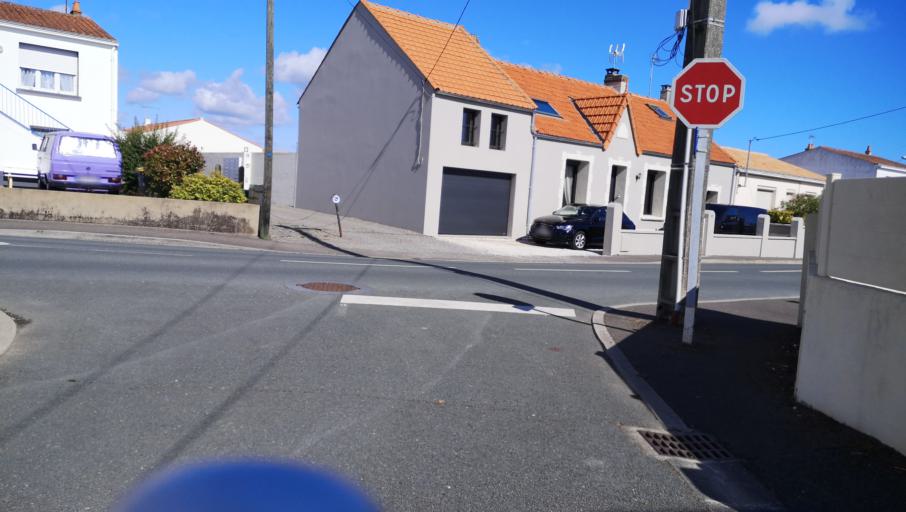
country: FR
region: Pays de la Loire
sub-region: Departement de la Vendee
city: Les Sables-d'Olonne
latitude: 46.5094
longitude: -1.7859
